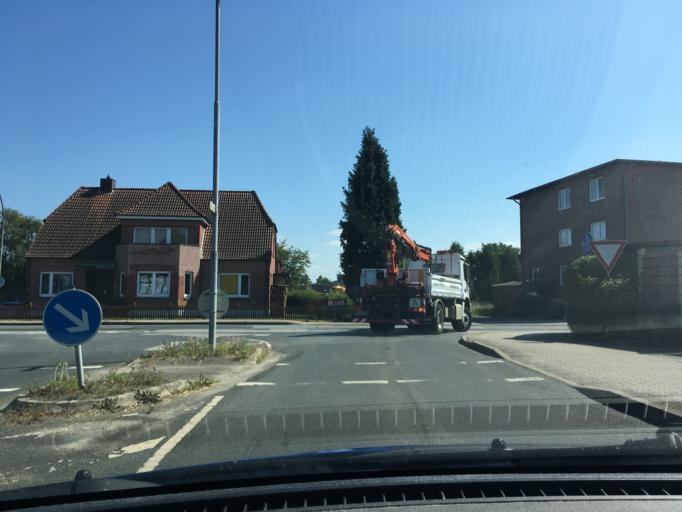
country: DE
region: Hamburg
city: Harburg
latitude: 53.4240
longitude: 10.0368
